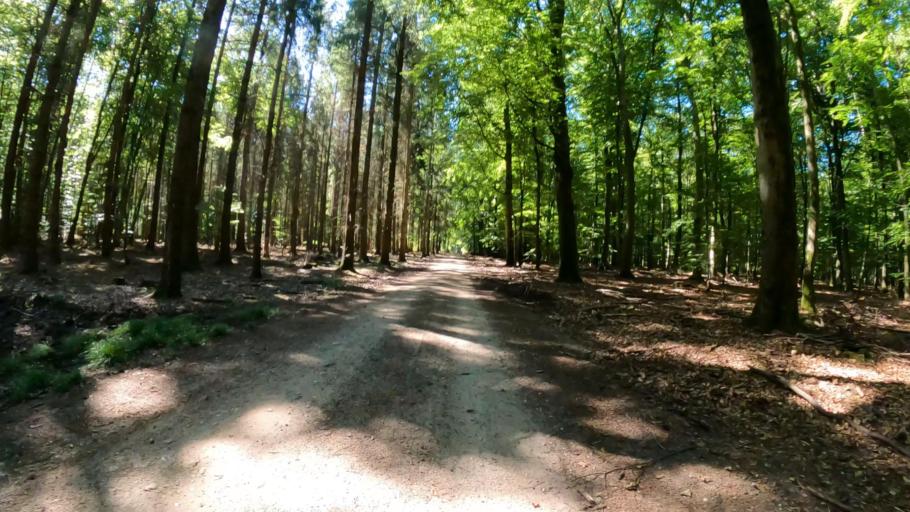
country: DE
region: Schleswig-Holstein
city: Kroppelshagen-Fahrendorf
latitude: 53.5027
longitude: 10.3384
